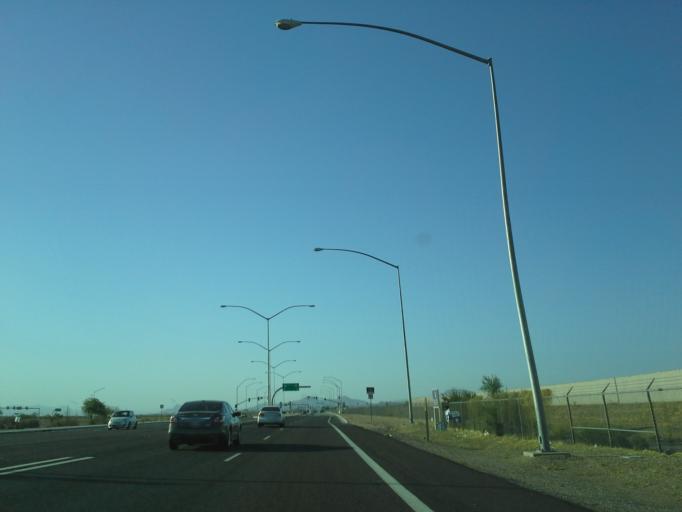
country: US
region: Arizona
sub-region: Maricopa County
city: Queen Creek
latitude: 33.3136
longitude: -111.6354
